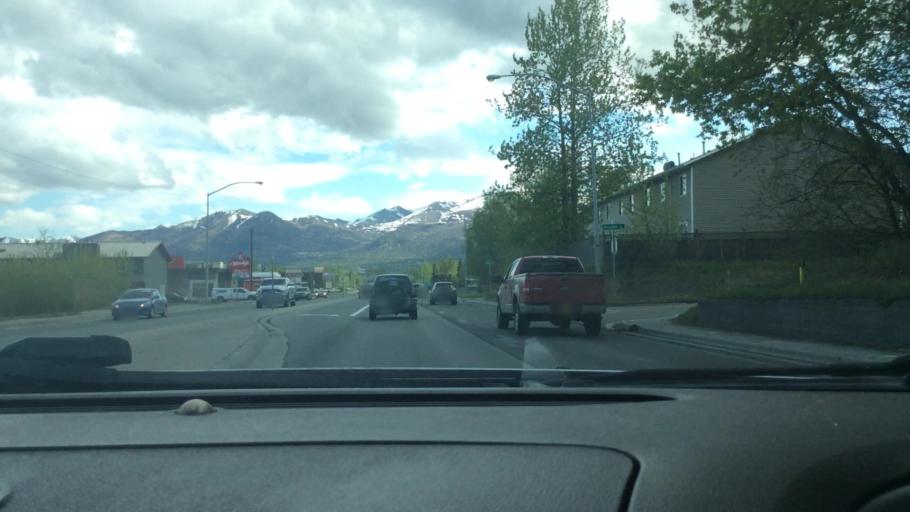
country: US
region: Alaska
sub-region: Anchorage Municipality
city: Anchorage
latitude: 61.1808
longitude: -149.8203
